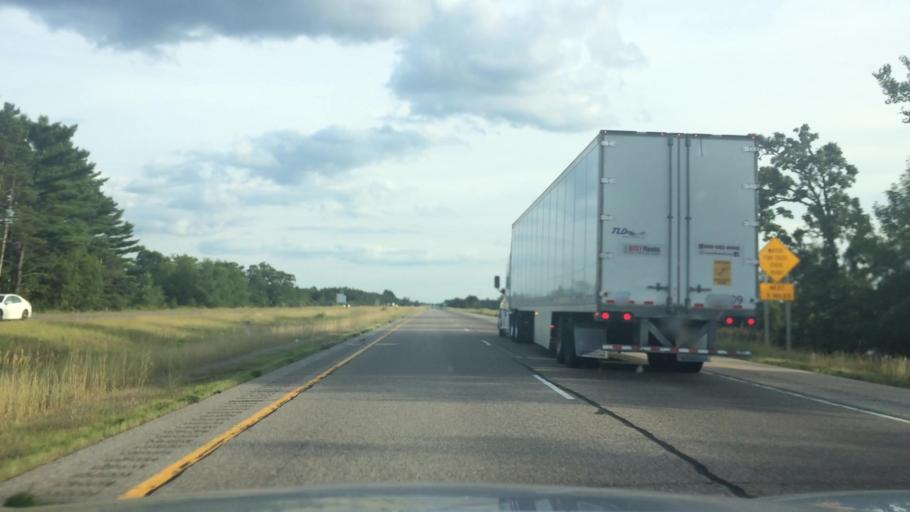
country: US
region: Wisconsin
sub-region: Portage County
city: Plover
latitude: 44.2441
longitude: -89.5243
